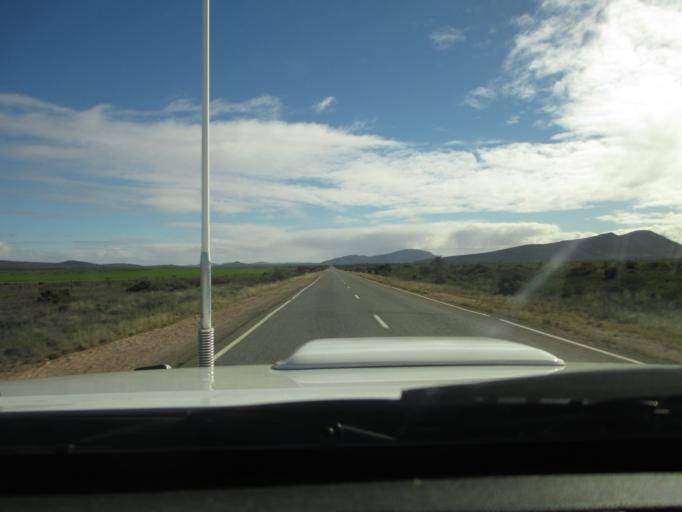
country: AU
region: South Australia
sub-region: Flinders Ranges
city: Quorn
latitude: -31.8727
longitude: 138.4097
